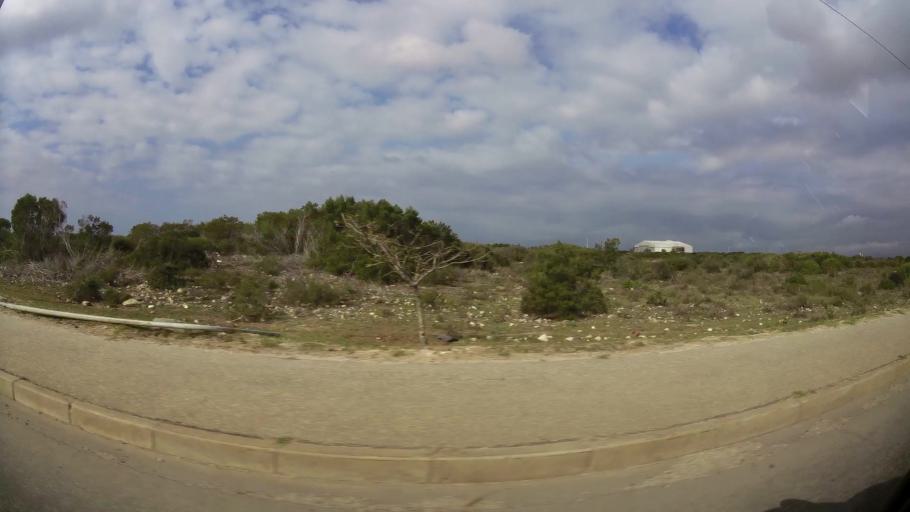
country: ZA
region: Eastern Cape
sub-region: Nelson Mandela Bay Metropolitan Municipality
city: Port Elizabeth
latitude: -33.8106
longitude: 25.6163
